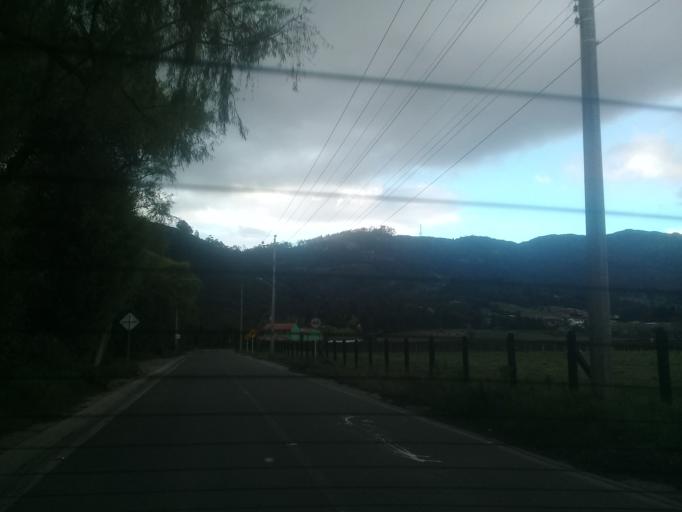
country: CO
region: Cundinamarca
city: Tabio
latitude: 4.9242
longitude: -74.0999
